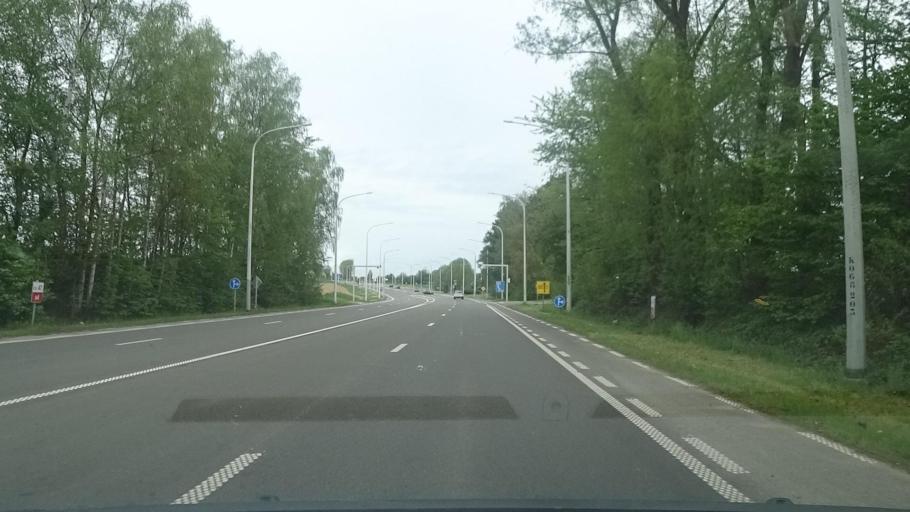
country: BE
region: Wallonia
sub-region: Province de Namur
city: Floreffe
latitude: 50.5115
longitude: 4.7744
